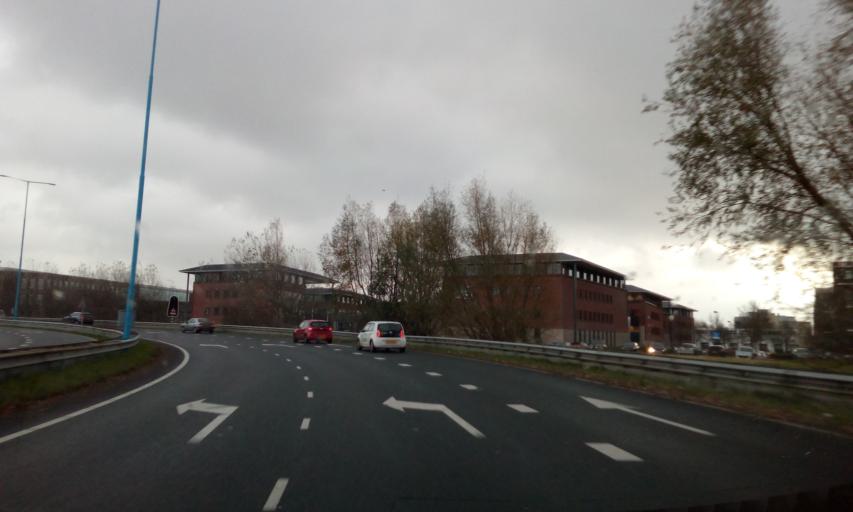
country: NL
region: South Holland
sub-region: Gemeente Zoetermeer
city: Zoetermeer
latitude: 52.0460
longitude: 4.4722
